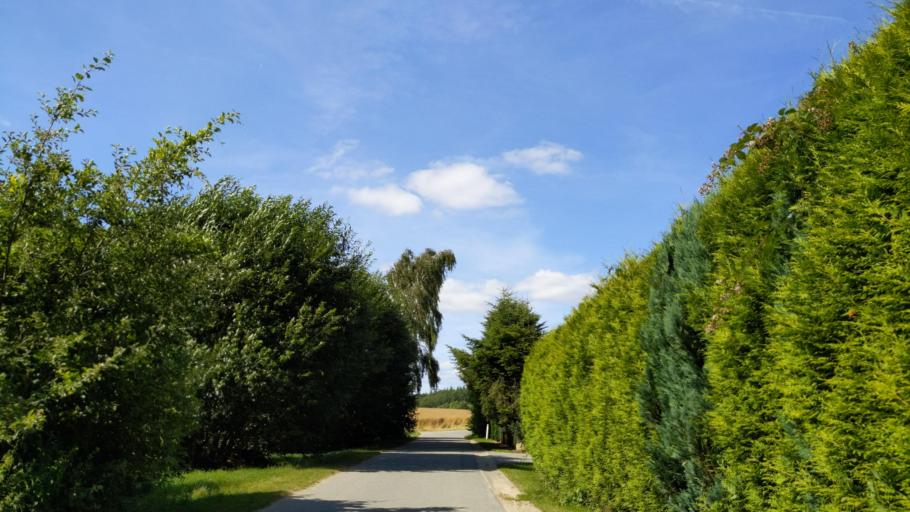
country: DE
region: Schleswig-Holstein
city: Kasseedorf
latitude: 54.1406
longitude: 10.7370
